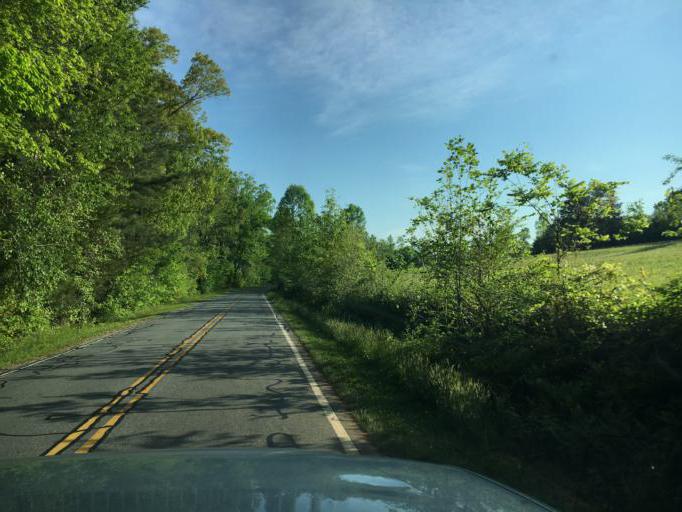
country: US
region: North Carolina
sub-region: Rutherford County
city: Rutherfordton
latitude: 35.3229
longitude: -81.9905
